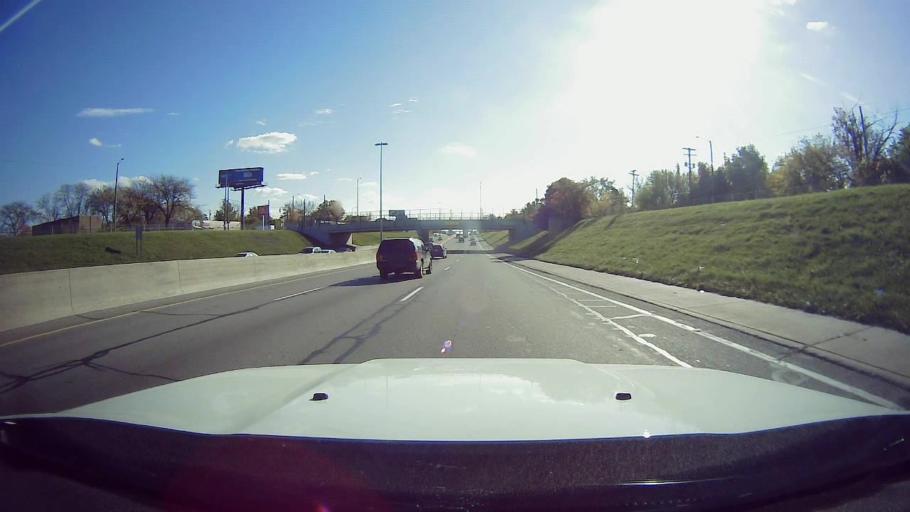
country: US
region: Michigan
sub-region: Wayne County
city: Dearborn
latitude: 42.3522
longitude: -83.2165
